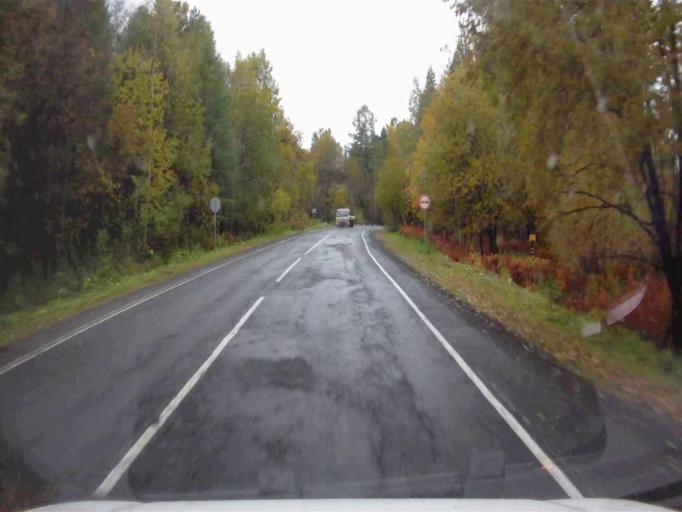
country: RU
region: Chelyabinsk
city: Verkhniy Ufaley
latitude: 56.0432
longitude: 60.0985
